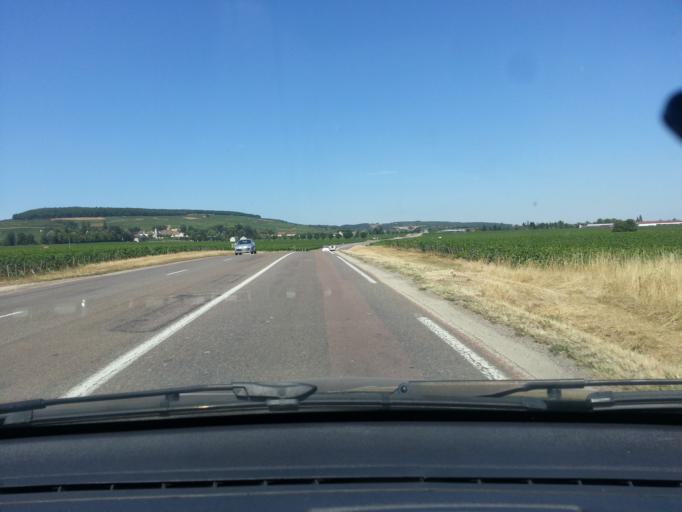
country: FR
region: Bourgogne
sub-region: Departement de la Cote-d'Or
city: Beaune
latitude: 47.0543
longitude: 4.8583
